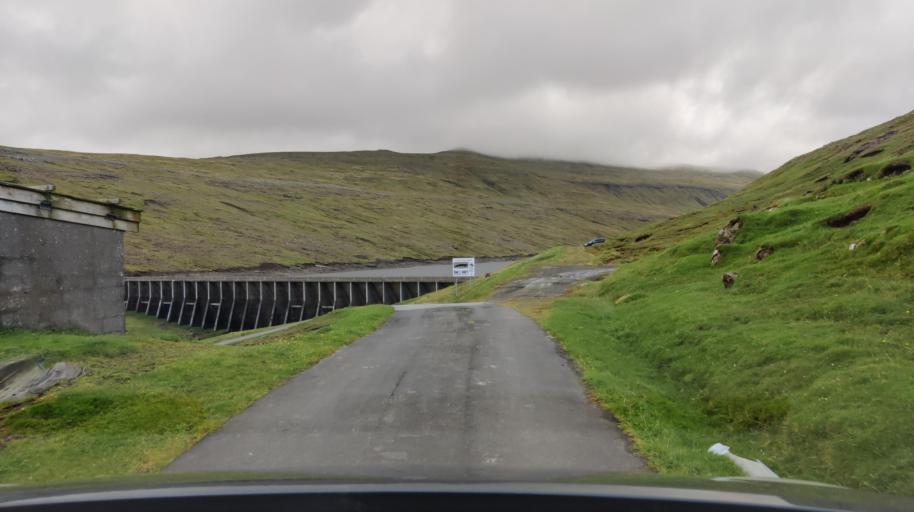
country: FO
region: Streymoy
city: Vestmanna
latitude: 62.1757
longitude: -7.1515
